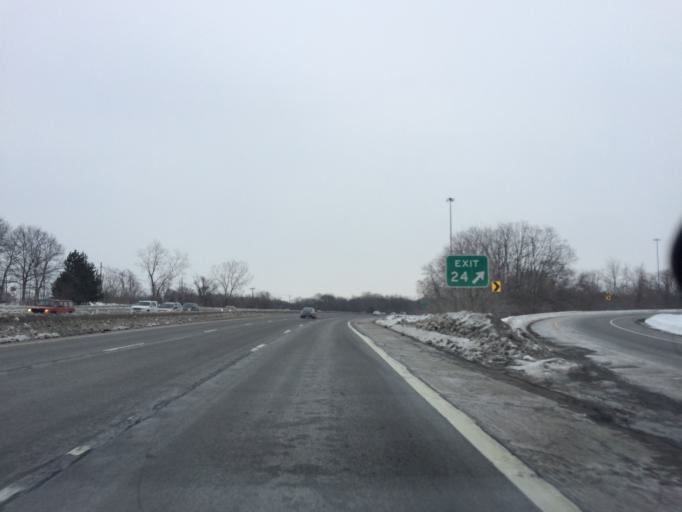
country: US
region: New York
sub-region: Monroe County
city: East Rochester
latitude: 43.1190
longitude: -77.5120
